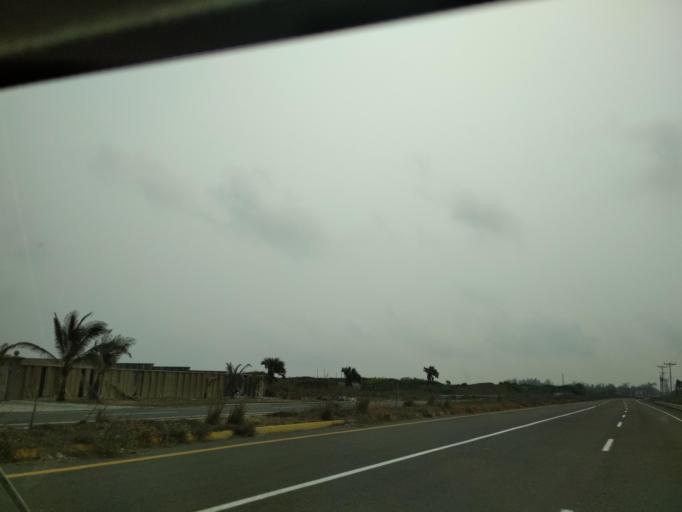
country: MX
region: Veracruz
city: Anton Lizardo
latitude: 19.0530
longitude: -96.0279
